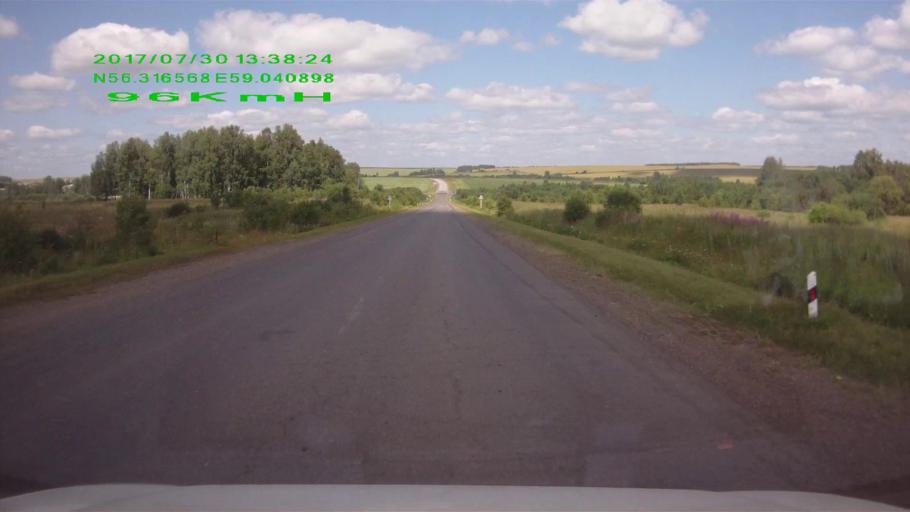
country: RU
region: Sverdlovsk
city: Mikhaylovsk
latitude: 56.3170
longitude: 59.0410
